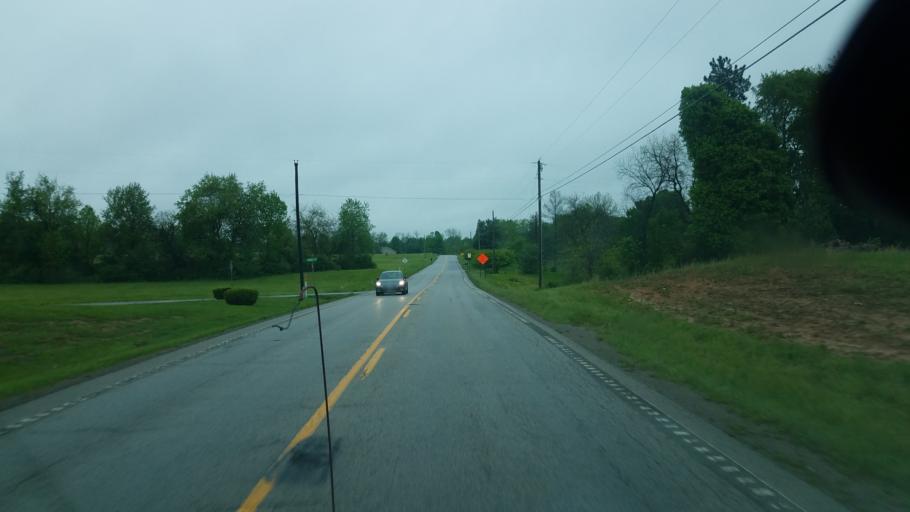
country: US
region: Ohio
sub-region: Highland County
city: Hillsboro
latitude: 39.2567
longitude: -83.6008
